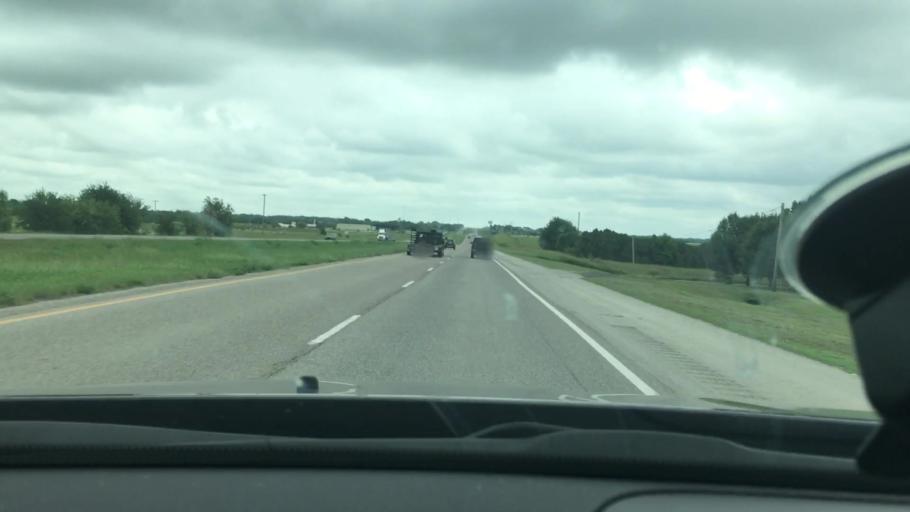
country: US
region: Oklahoma
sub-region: Murray County
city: Davis
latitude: 34.5060
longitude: -97.0854
